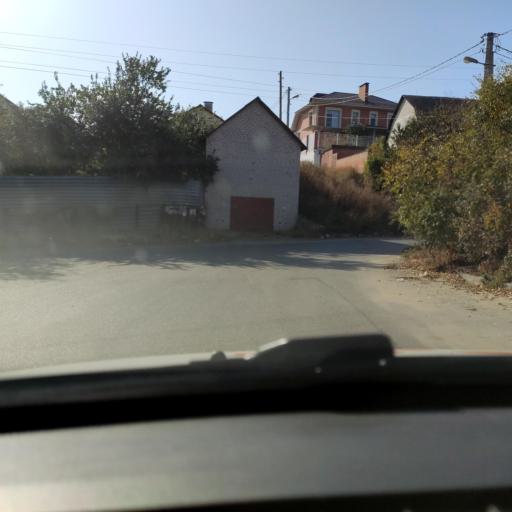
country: RU
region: Voronezj
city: Voronezh
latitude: 51.6301
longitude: 39.1975
